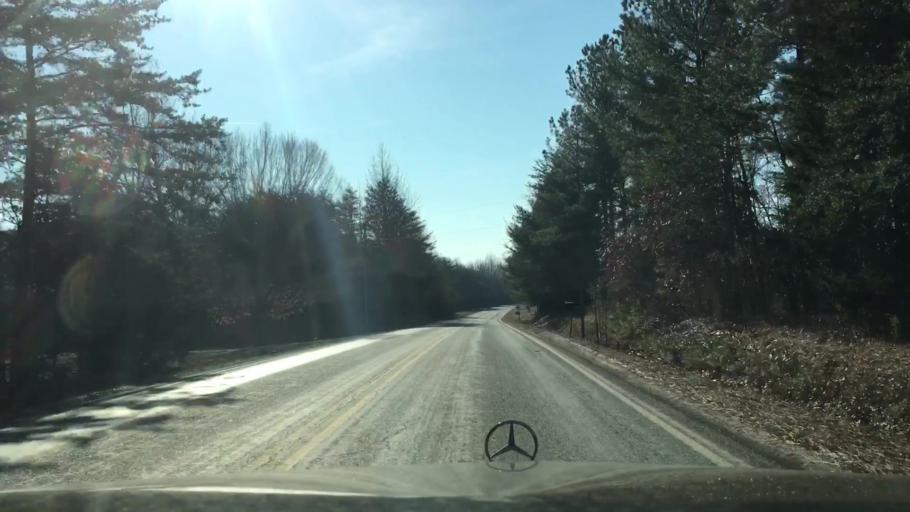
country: US
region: Virginia
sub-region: Pittsylvania County
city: Motley
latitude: 37.1797
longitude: -79.4099
